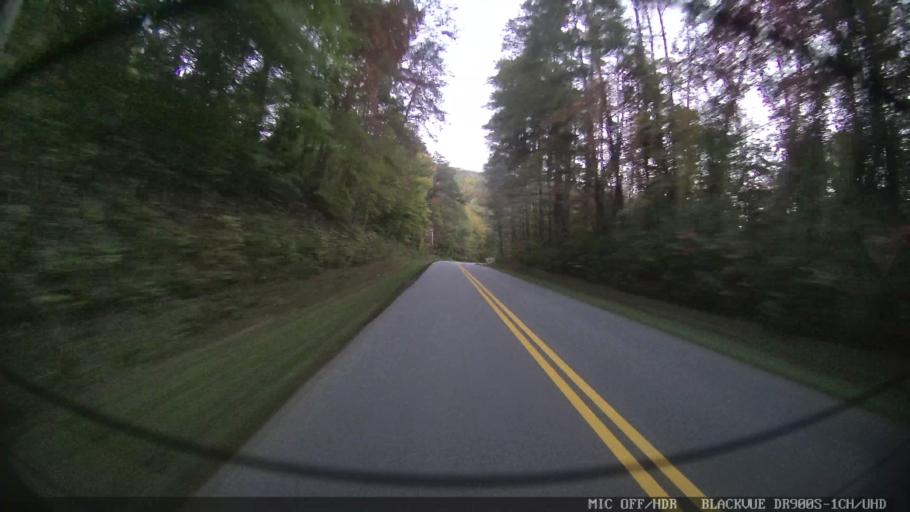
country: US
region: Georgia
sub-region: Union County
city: Blairsville
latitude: 34.8946
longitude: -83.8688
